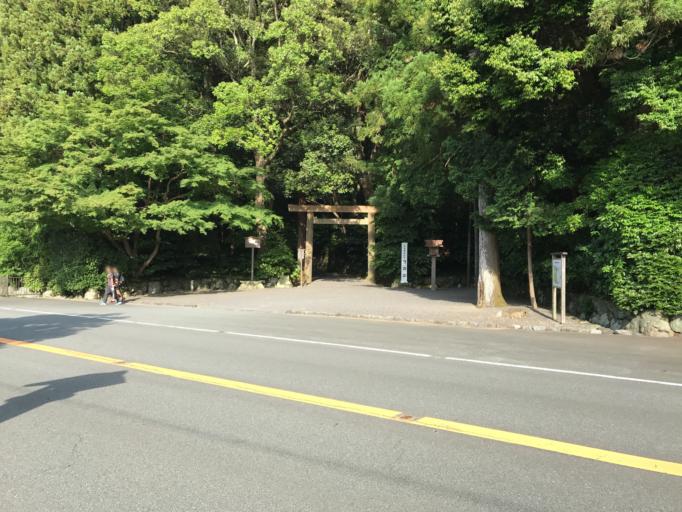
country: JP
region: Mie
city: Ise
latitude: 34.4730
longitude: 136.7266
